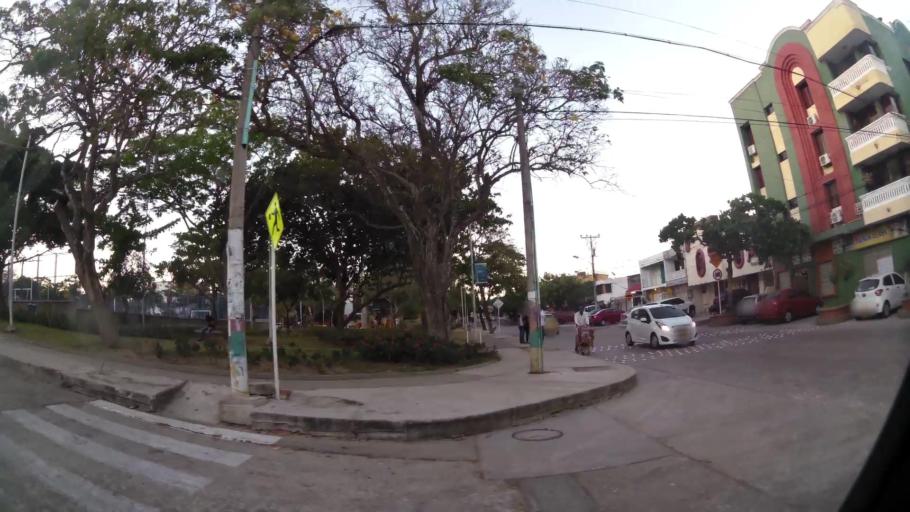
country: CO
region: Atlantico
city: Barranquilla
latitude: 10.9798
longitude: -74.8090
